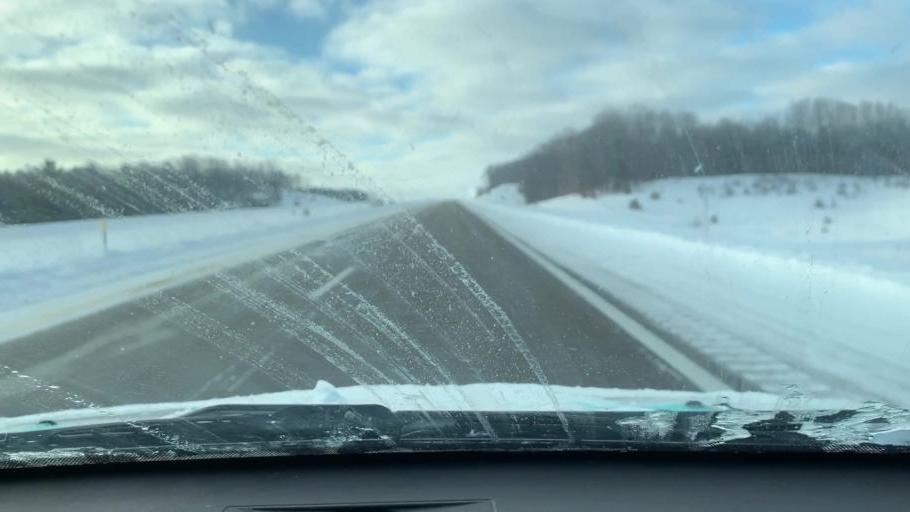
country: US
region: Michigan
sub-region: Wexford County
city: Manton
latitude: 44.3557
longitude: -85.4038
